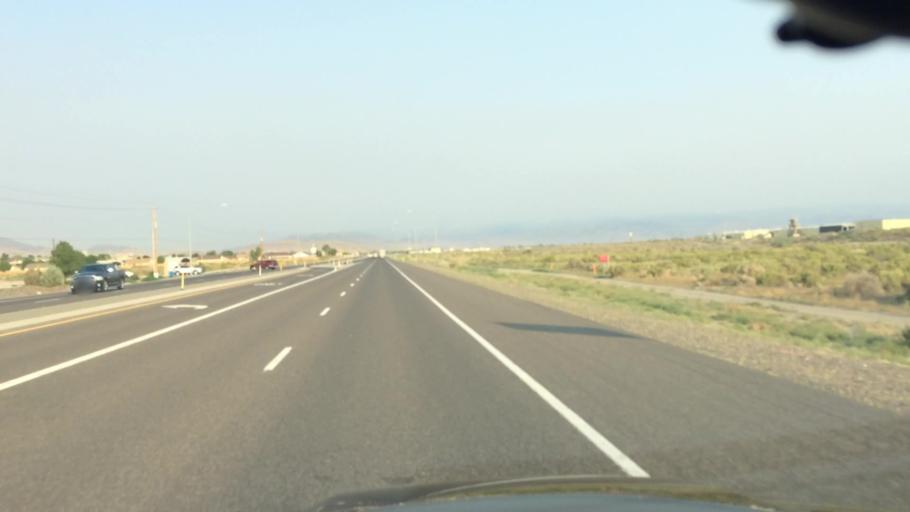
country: US
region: Nevada
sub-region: Lyon County
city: Fernley
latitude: 39.5982
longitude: -119.1958
